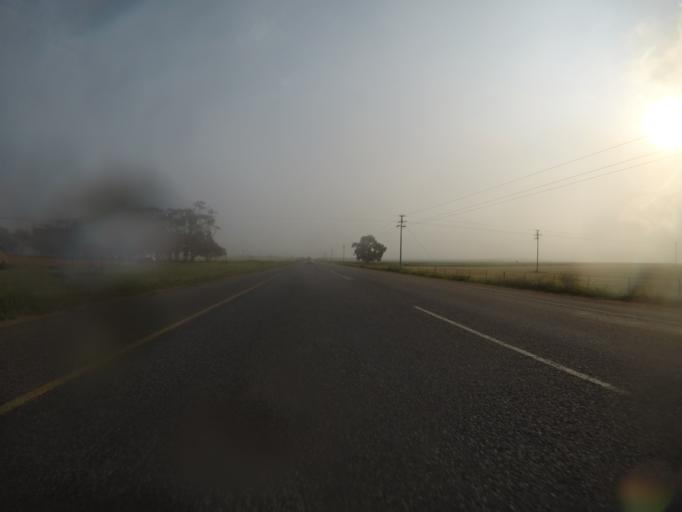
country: ZA
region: Western Cape
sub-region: City of Cape Town
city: Kraaifontein
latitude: -33.6669
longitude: 18.7075
